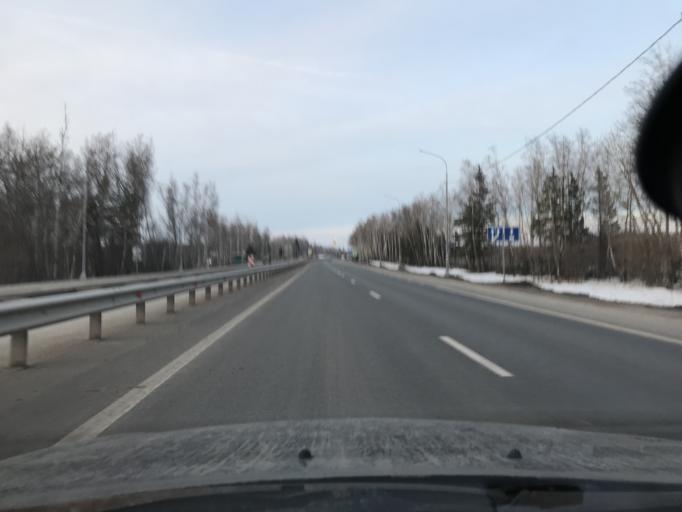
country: RU
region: Kaluga
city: Kaluga
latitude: 54.6309
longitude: 36.2921
